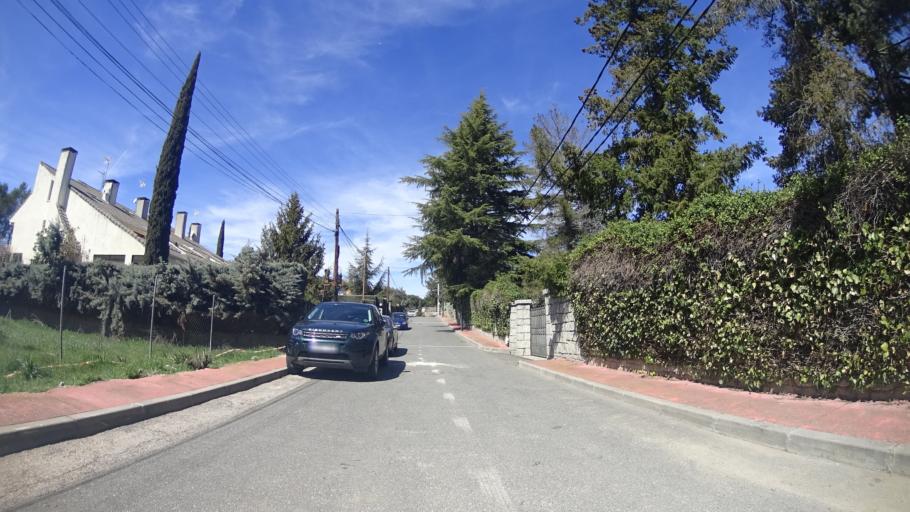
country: ES
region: Madrid
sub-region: Provincia de Madrid
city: Galapagar
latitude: 40.5901
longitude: -3.9867
